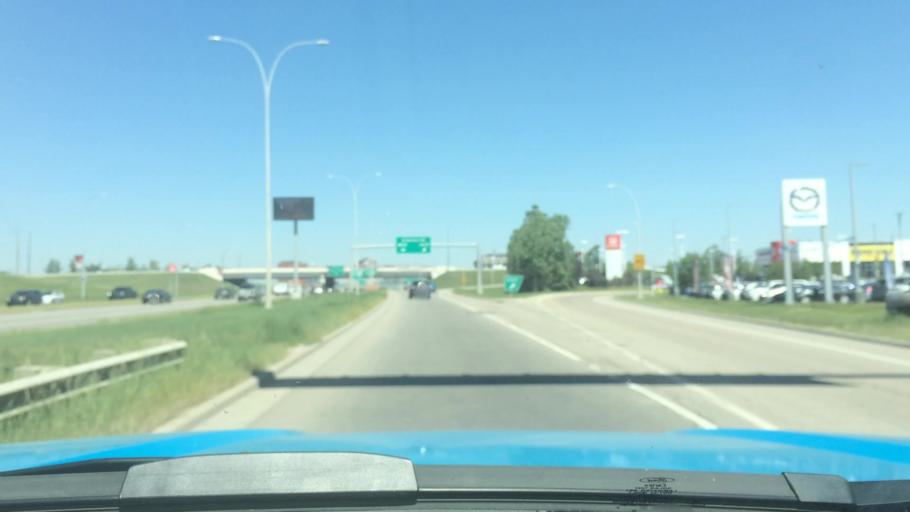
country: CA
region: Alberta
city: Calgary
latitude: 50.9476
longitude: -114.0704
